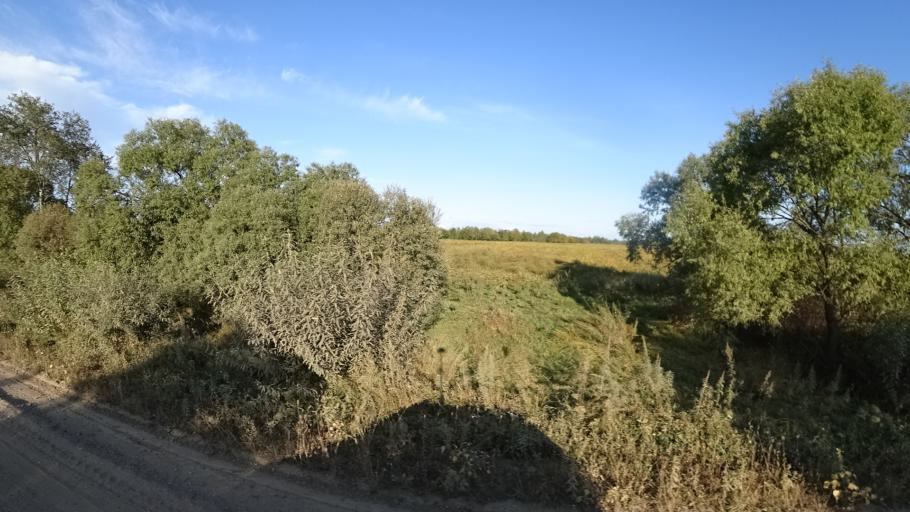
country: RU
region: Amur
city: Arkhara
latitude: 49.3567
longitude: 130.1374
